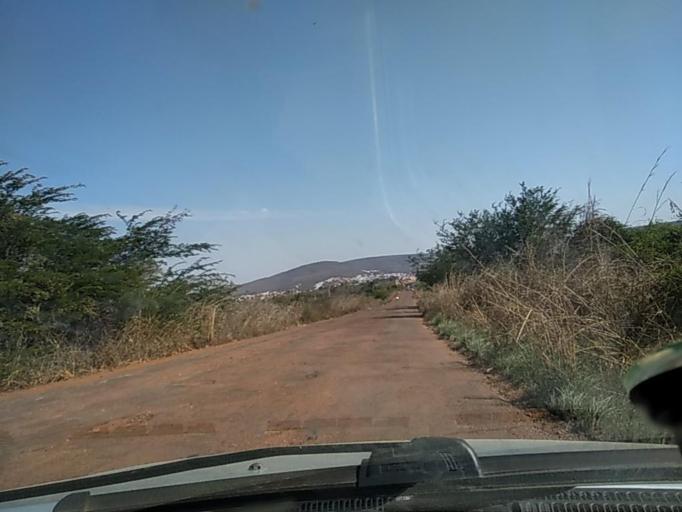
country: BR
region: Bahia
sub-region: Caetite
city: Caetite
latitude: -14.0313
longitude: -42.4872
